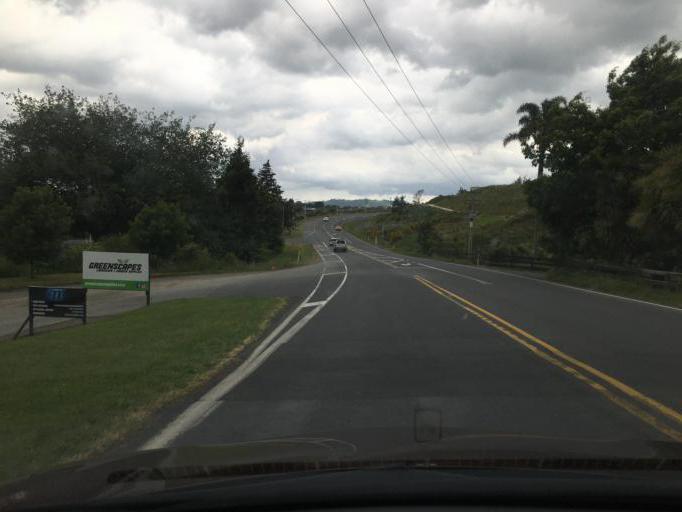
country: NZ
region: Waikato
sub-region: Waipa District
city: Cambridge
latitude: -37.9006
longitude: 175.4547
